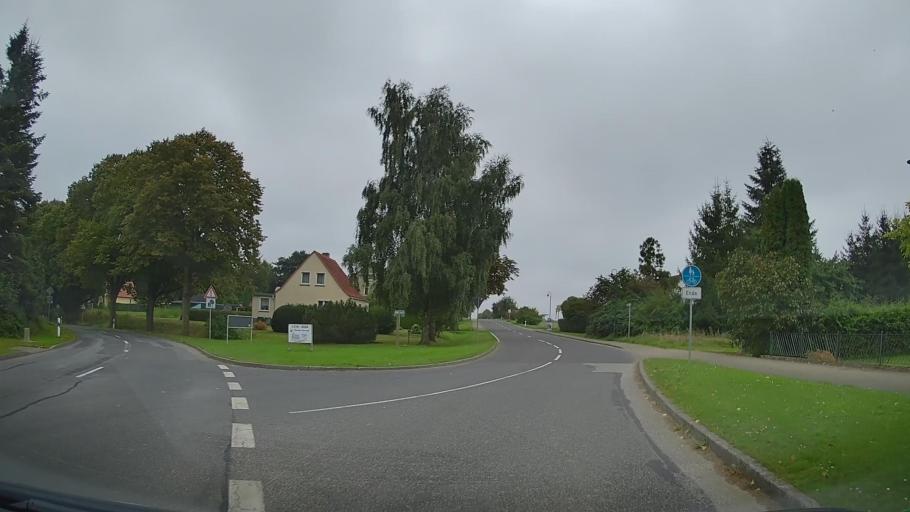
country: DE
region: Mecklenburg-Vorpommern
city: Schwaan
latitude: 53.9085
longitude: 12.1949
